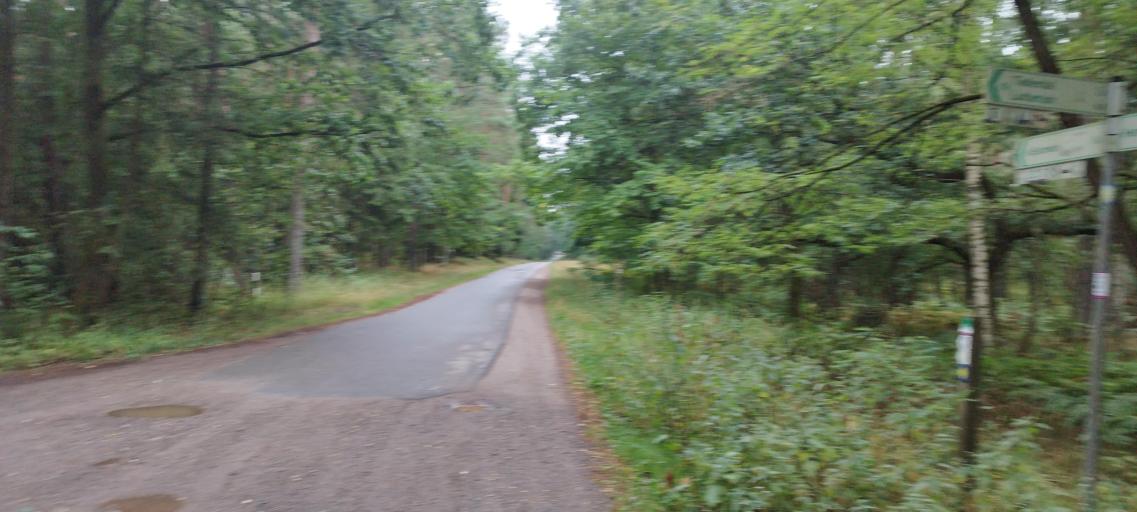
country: DE
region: Lower Saxony
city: Hermannsburg
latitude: 52.7963
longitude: 10.1255
